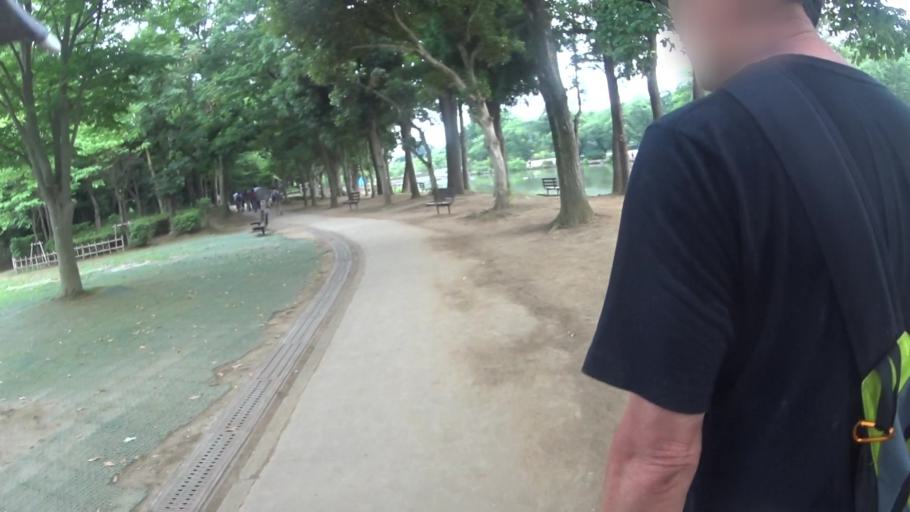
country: JP
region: Saitama
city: Okegawa
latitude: 35.9557
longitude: 139.5480
